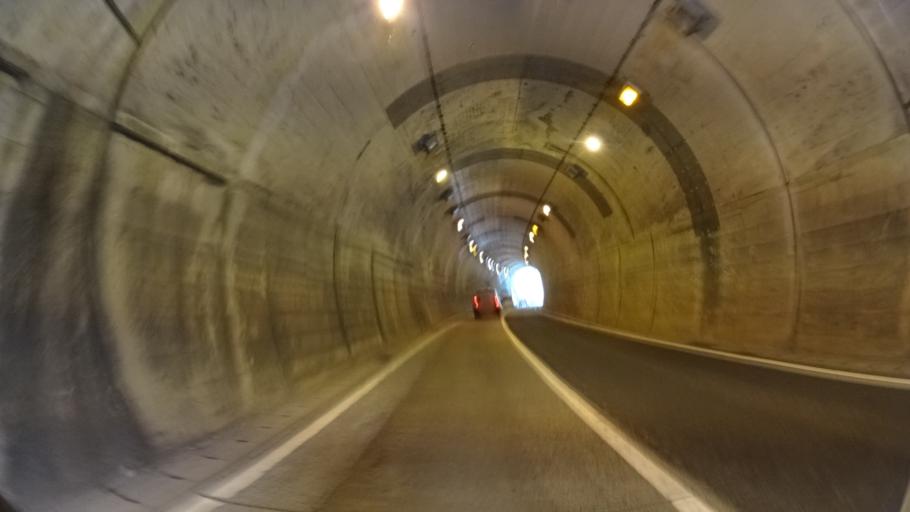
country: JP
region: Ehime
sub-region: Shikoku-chuo Shi
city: Matsuyama
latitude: 33.8793
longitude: 132.8359
